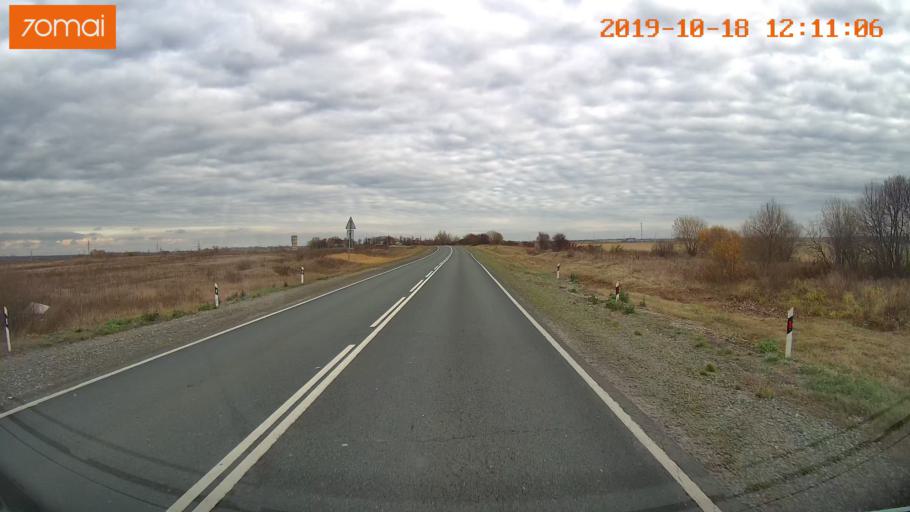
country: RU
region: Rjazan
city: Zakharovo
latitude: 54.3981
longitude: 39.3452
